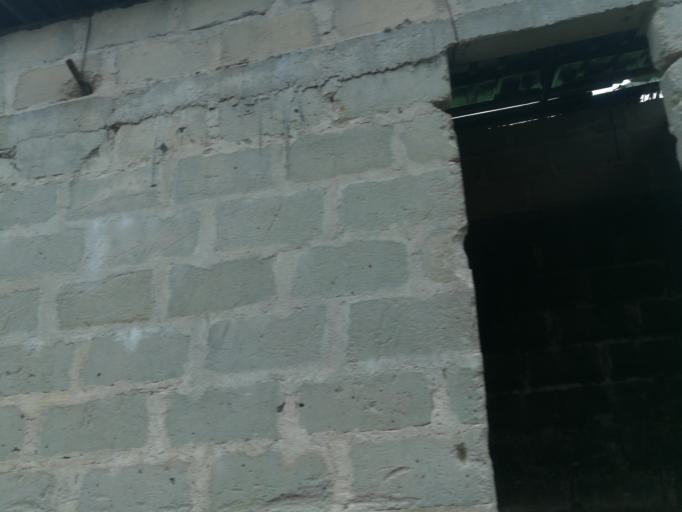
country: NG
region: Rivers
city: Port Harcourt
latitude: 4.7978
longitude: 6.9543
